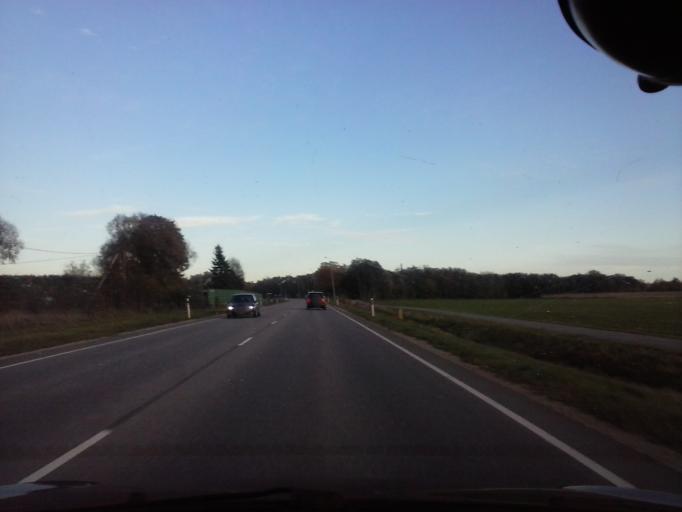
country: EE
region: Laeaene
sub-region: Ridala Parish
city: Uuemoisa
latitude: 58.9715
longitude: 23.8711
